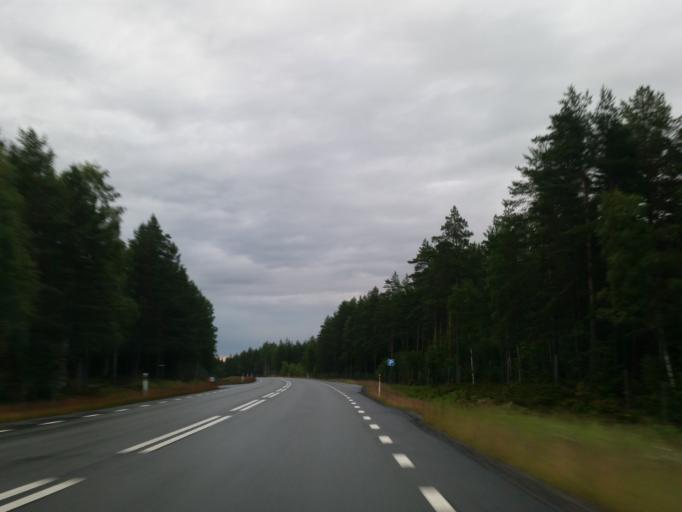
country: SE
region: Vaesterbotten
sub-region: Robertsfors Kommun
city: Robertsfors
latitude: 64.0222
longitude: 20.8395
